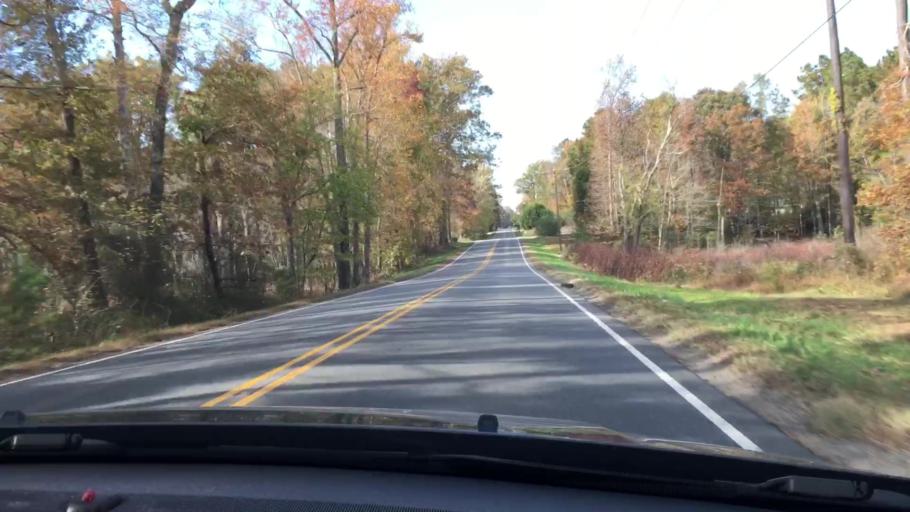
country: US
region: Virginia
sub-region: King William County
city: West Point
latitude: 37.5687
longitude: -76.8332
